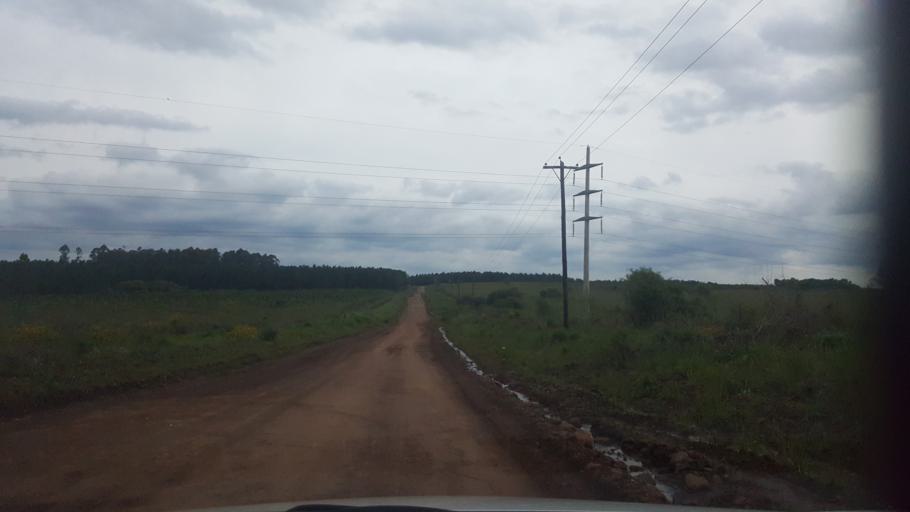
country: AR
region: Misiones
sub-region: Departamento de Candelaria
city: Candelaria
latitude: -27.5035
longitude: -55.7368
